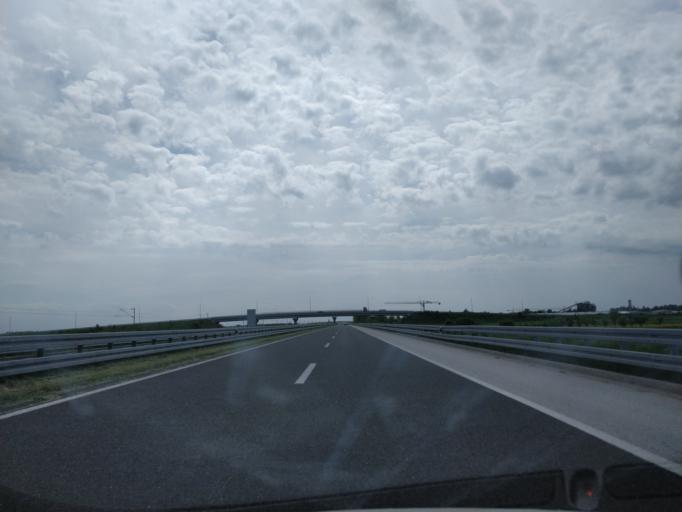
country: HR
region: Grad Zagreb
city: Odra
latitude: 45.7285
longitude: 16.0184
